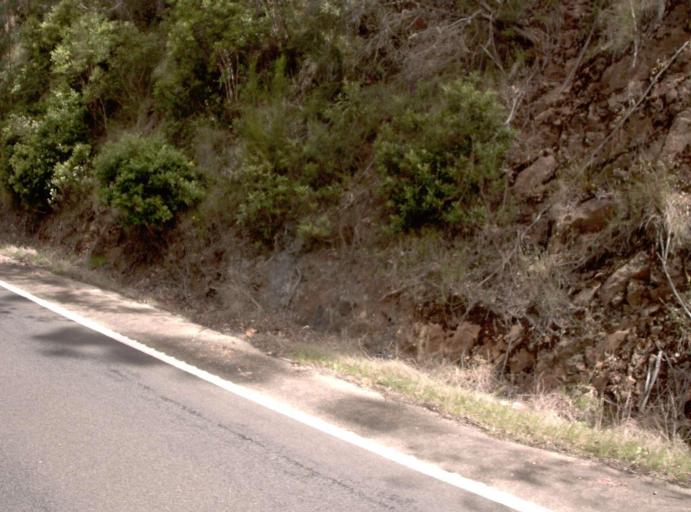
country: AU
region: New South Wales
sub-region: Bombala
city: Bombala
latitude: -37.5355
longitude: 149.3807
